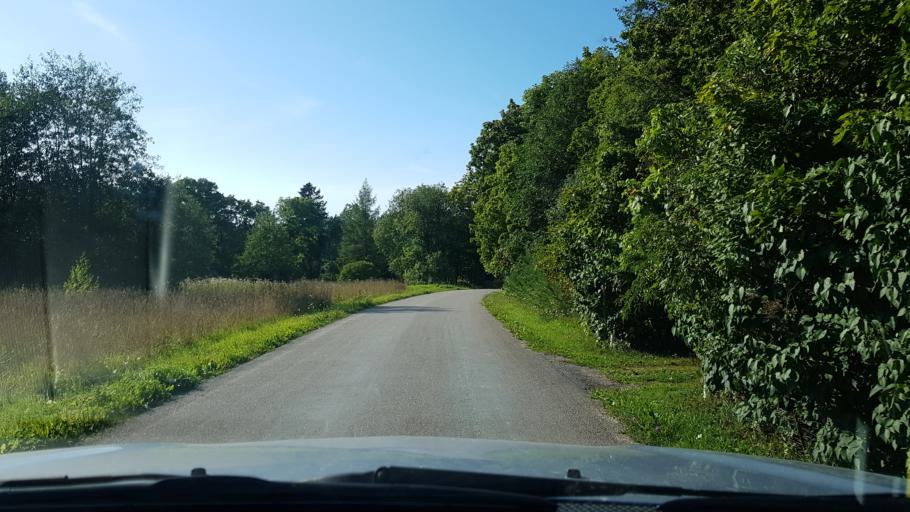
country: EE
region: Ida-Virumaa
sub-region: Narva-Joesuu linn
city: Narva-Joesuu
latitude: 59.4073
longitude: 27.9914
